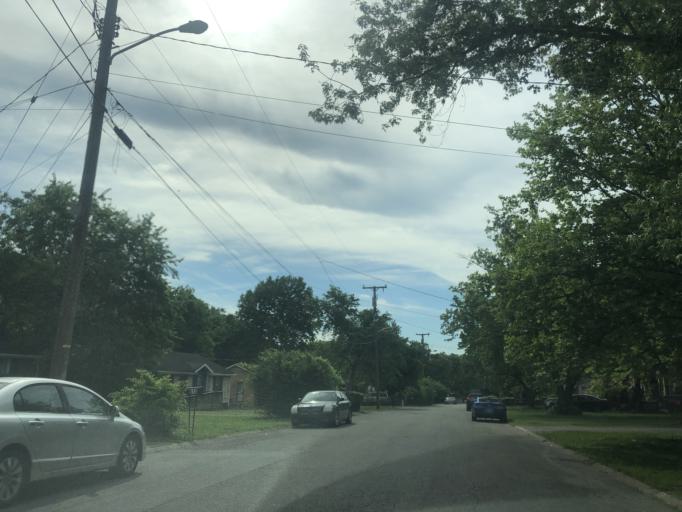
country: US
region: Tennessee
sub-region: Davidson County
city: Nashville
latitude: 36.2200
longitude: -86.8084
